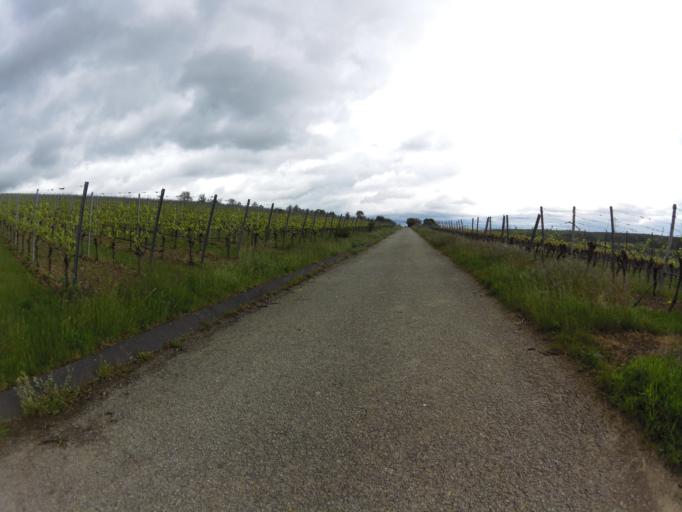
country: DE
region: Bavaria
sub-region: Regierungsbezirk Unterfranken
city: Sommerach
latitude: 49.8355
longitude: 10.2164
